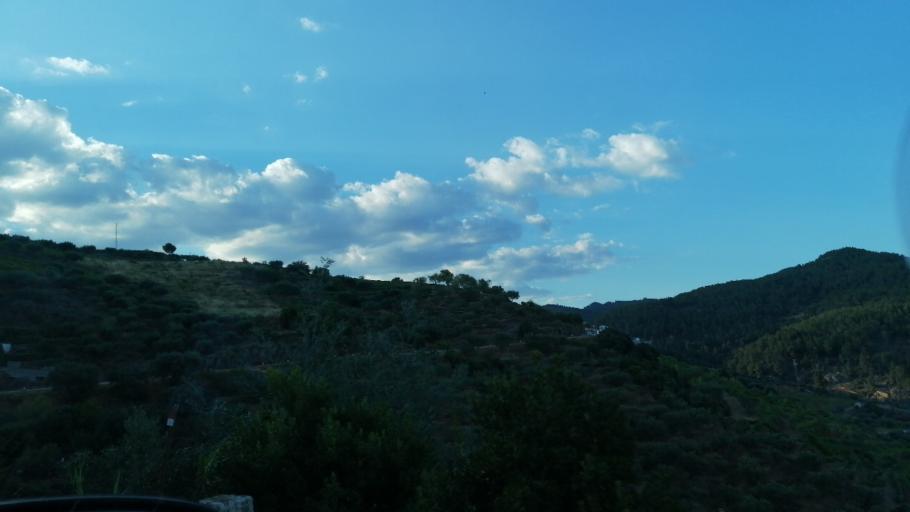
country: PT
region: Viseu
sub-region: Sao Joao da Pesqueira
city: Sao Joao da Pesqueira
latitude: 41.2403
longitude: -7.4317
